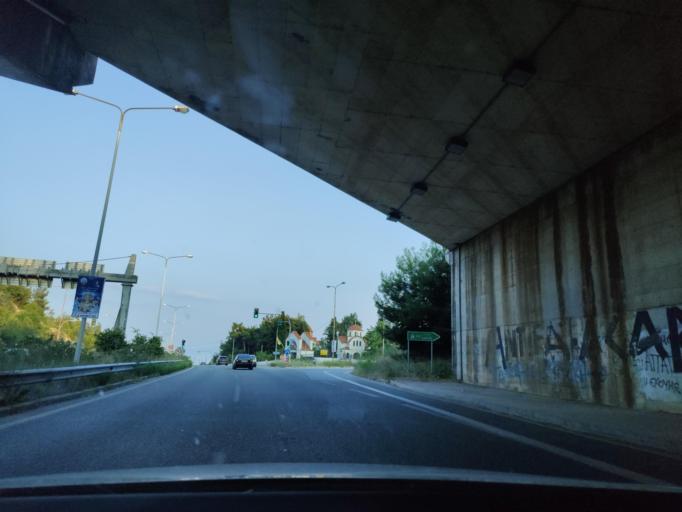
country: GR
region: East Macedonia and Thrace
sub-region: Nomos Kavalas
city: Amygdaleonas
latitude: 40.9425
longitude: 24.3752
